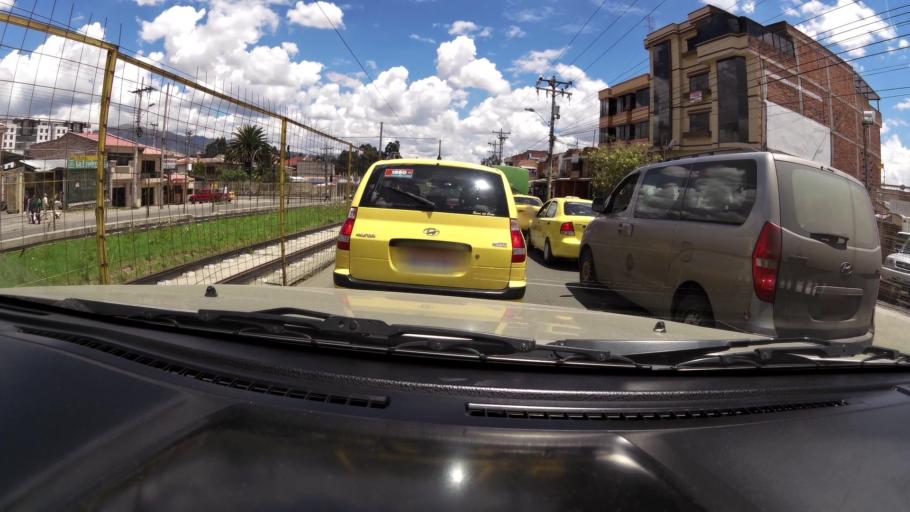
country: EC
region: Azuay
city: Cuenca
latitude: -2.9099
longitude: -79.0350
